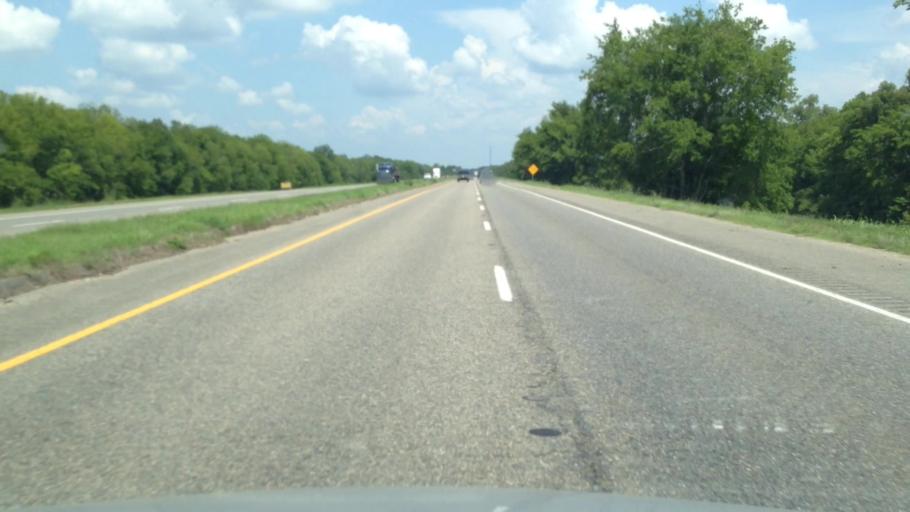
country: US
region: Louisiana
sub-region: Saint Landry Parish
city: Krotz Springs
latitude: 30.5435
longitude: -91.7990
